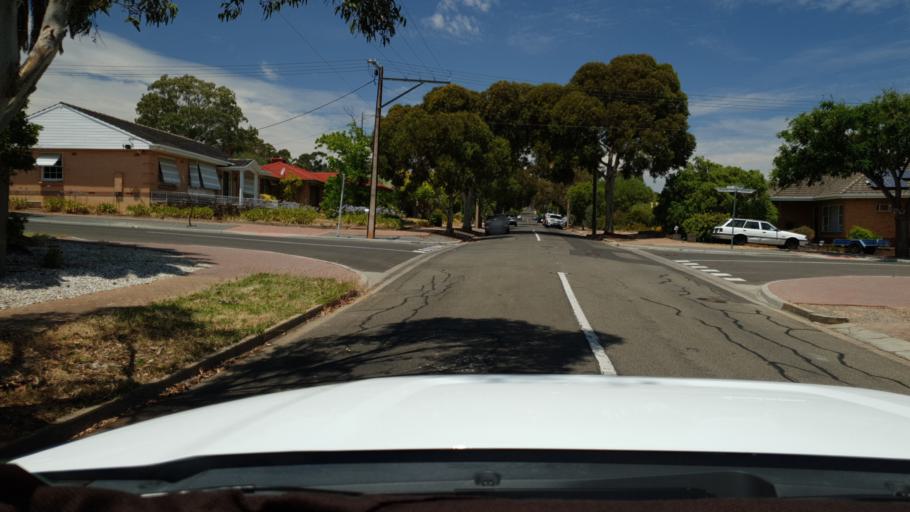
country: AU
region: South Australia
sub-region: Marion
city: Clovelly Park
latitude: -35.0070
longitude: 138.5836
